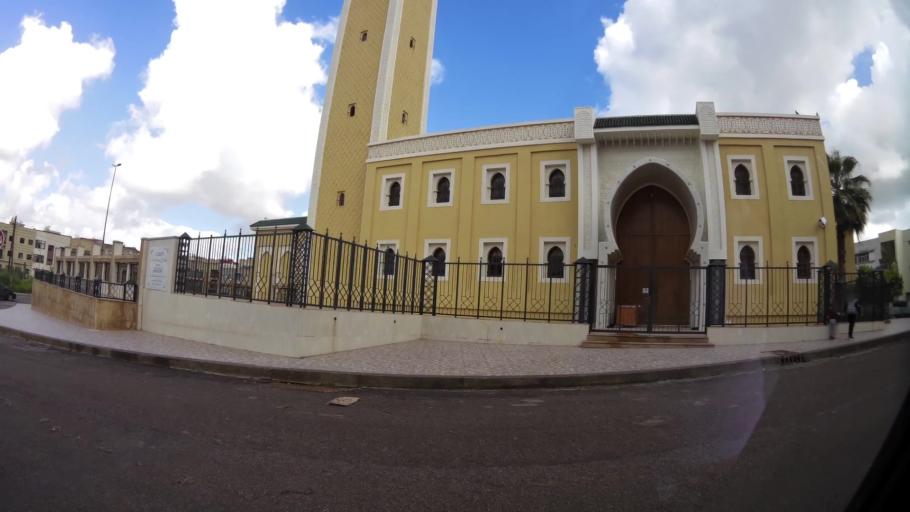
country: MA
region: Grand Casablanca
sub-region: Mediouna
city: Tit Mellil
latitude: 33.5456
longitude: -7.4882
